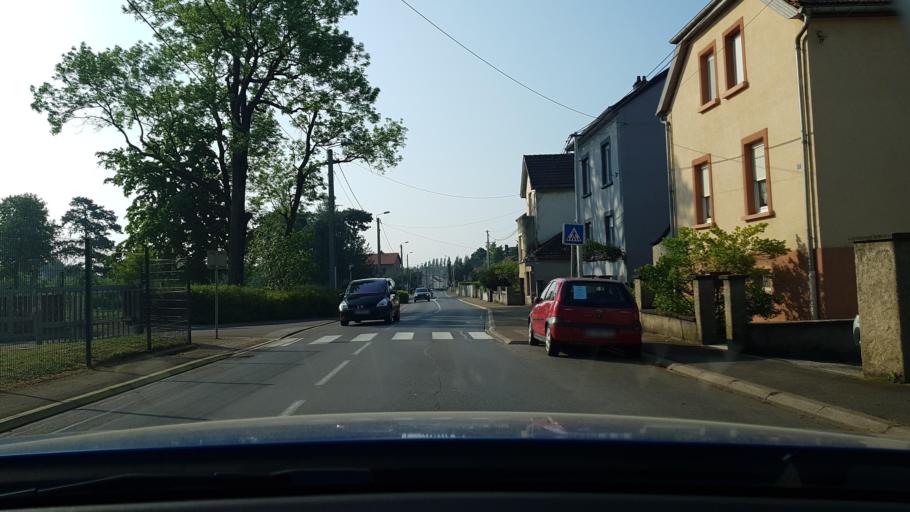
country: FR
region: Lorraine
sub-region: Departement de la Moselle
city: Florange
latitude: 49.3320
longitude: 6.1137
